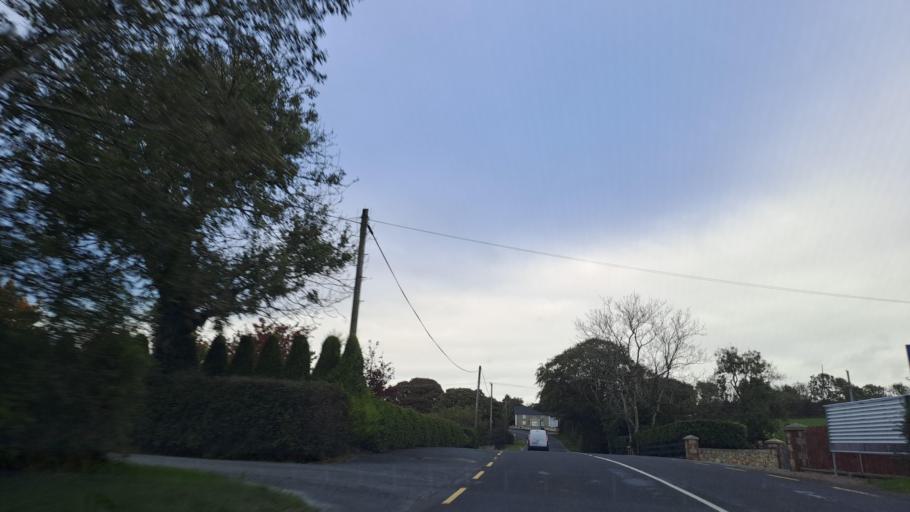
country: IE
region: Ulster
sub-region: An Cabhan
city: Cootehill
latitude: 54.0697
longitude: -6.9306
